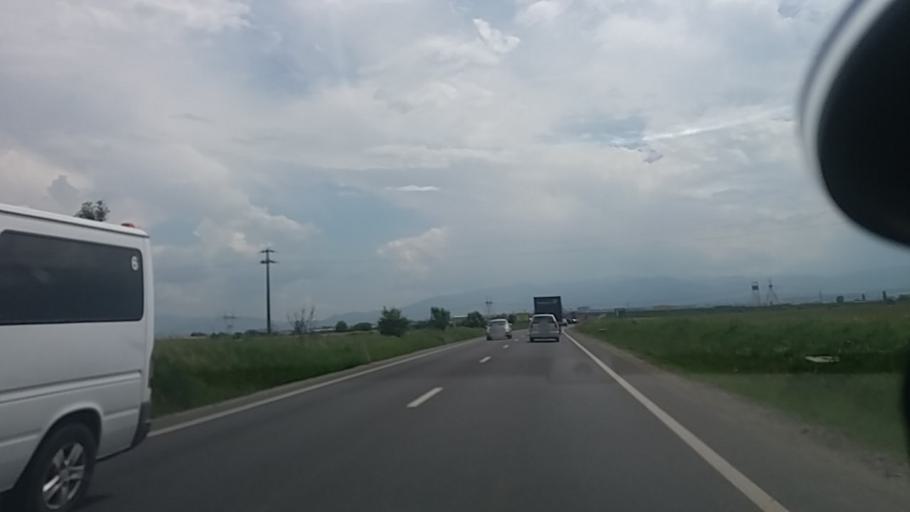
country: RO
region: Sibiu
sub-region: Comuna Sura Mare
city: Sura Mare
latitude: 45.8314
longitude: 24.1523
